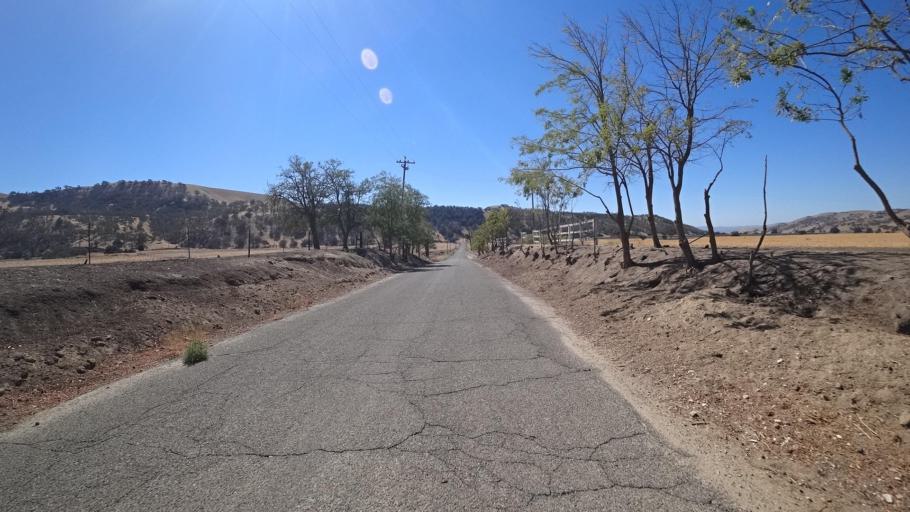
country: US
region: California
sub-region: San Luis Obispo County
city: San Miguel
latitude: 35.8246
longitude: -120.6548
